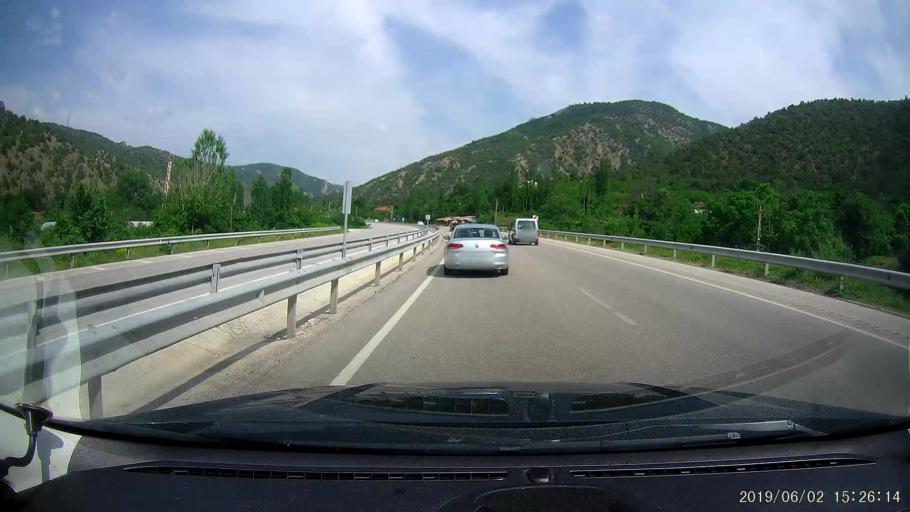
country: TR
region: Amasya
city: Saraycik
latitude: 40.9870
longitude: 35.0327
